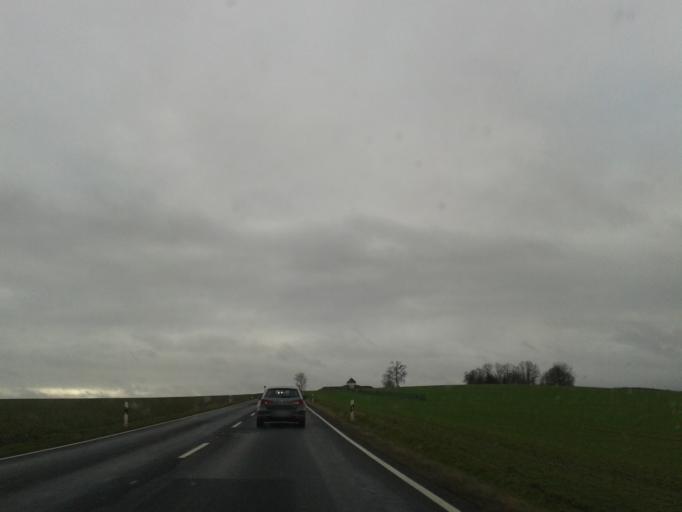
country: DE
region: Saxony
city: Grossschweidnitz
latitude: 51.0634
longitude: 14.6463
